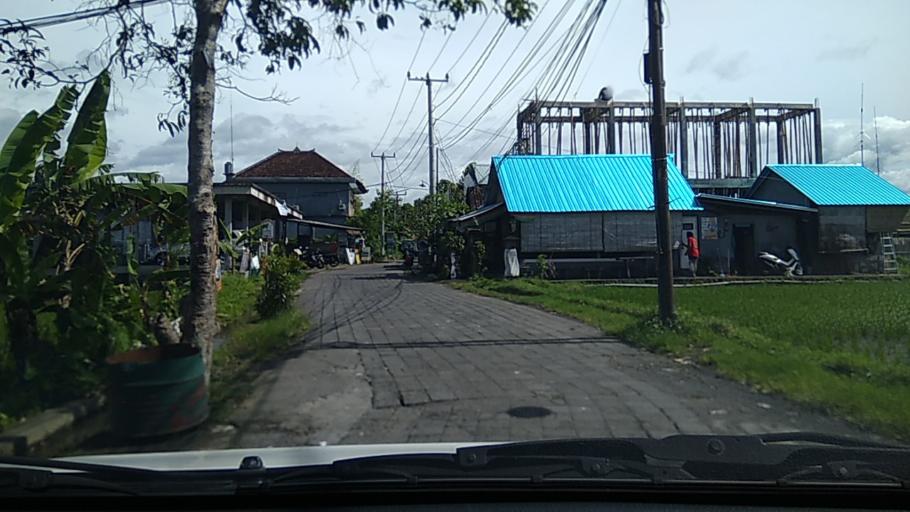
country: ID
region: Bali
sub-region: Kabupaten Gianyar
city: Ubud
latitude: -8.5101
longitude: 115.2585
